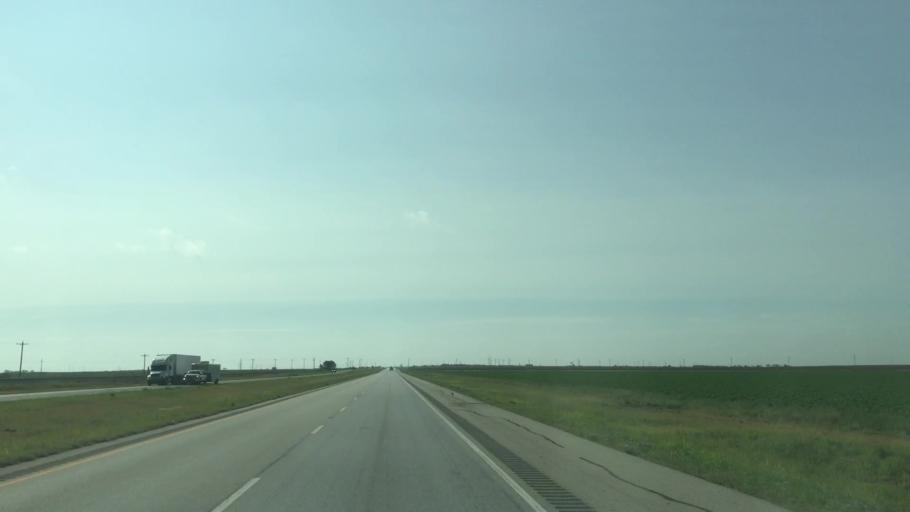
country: US
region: Texas
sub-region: Scurry County
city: Snyder
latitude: 32.6648
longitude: -100.7932
